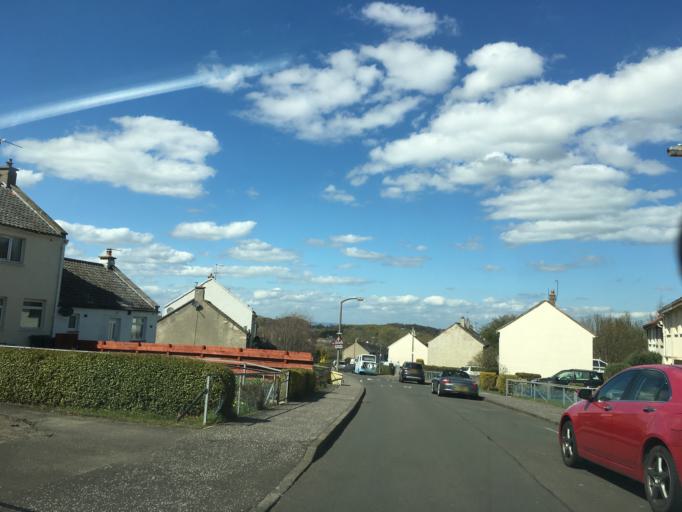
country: GB
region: Scotland
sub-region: Edinburgh
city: Colinton
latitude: 55.9050
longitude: -3.2190
